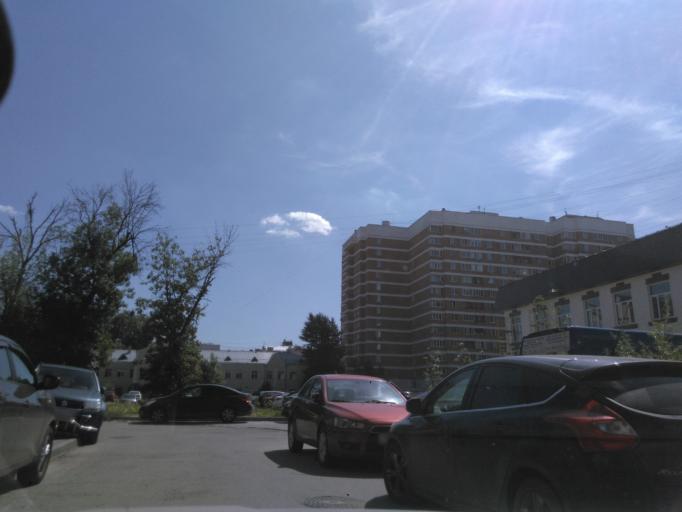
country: RU
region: Moscow
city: Zamoskvorech'ye
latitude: 55.7223
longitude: 37.6236
